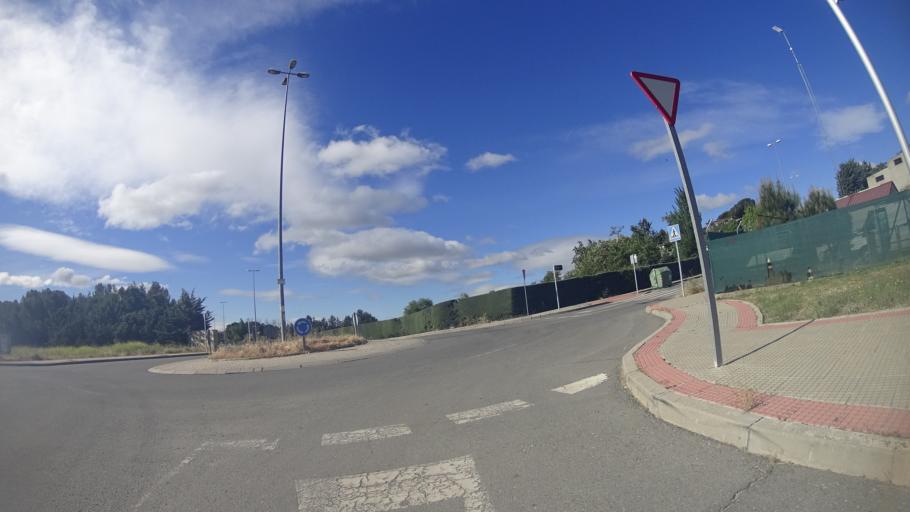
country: ES
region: Madrid
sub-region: Provincia de Madrid
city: Villanueva del Pardillo
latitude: 40.4914
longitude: -3.9408
